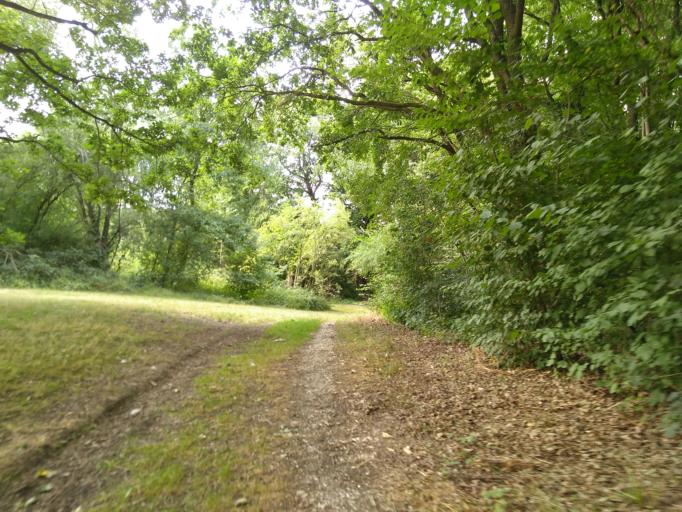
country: DE
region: North Rhine-Westphalia
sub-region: Regierungsbezirk Koln
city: Alfter
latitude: 50.7018
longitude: 7.0362
